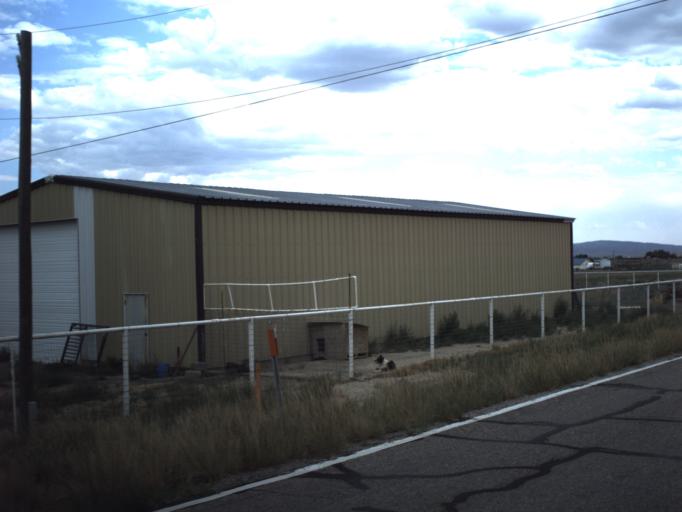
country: US
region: Utah
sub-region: Emery County
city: Huntington
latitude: 39.4054
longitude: -110.8526
